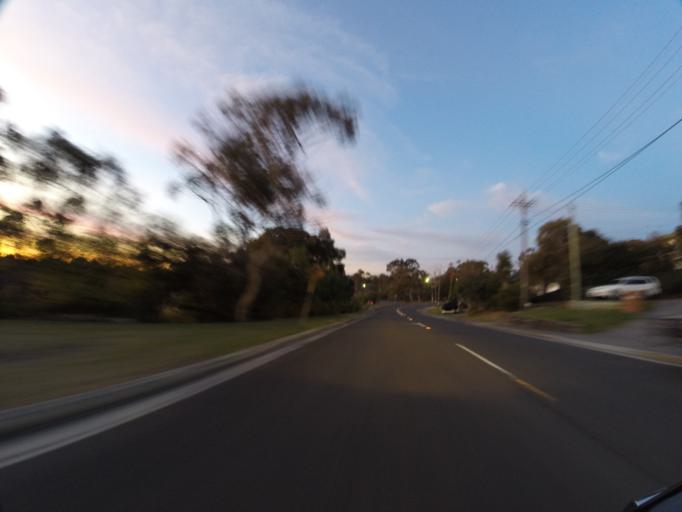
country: AU
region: New South Wales
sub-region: Sutherland Shire
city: Heathcote
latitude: -34.0901
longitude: 151.0018
